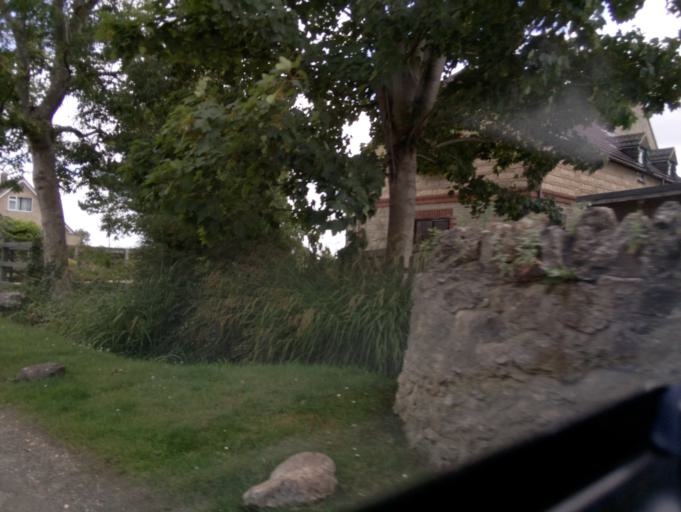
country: GB
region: England
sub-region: Oxfordshire
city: Faringdon
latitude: 51.6172
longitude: -1.6057
